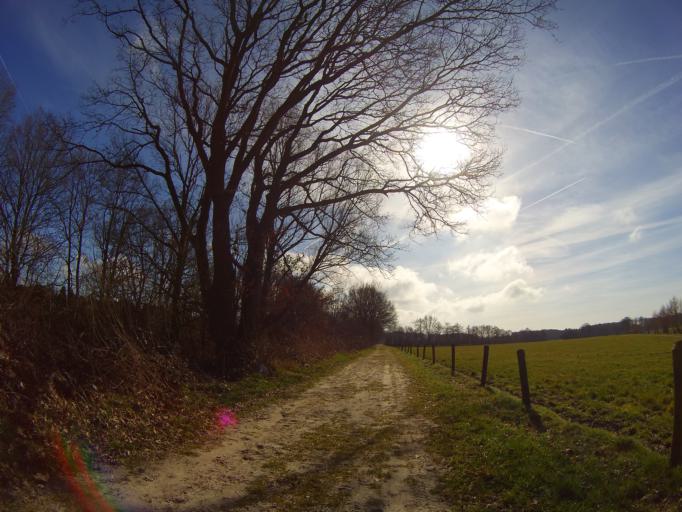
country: NL
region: Utrecht
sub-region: Gemeente Woudenberg
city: Woudenberg
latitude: 52.1050
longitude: 5.4278
